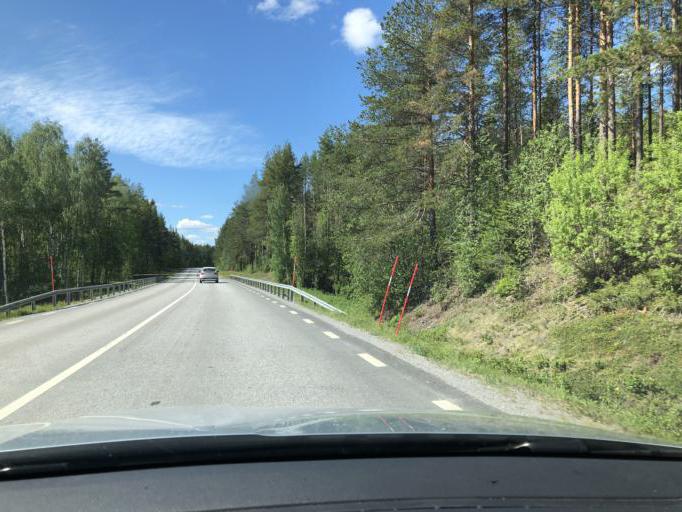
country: SE
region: Norrbotten
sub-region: Alvsbyns Kommun
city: AElvsbyn
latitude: 65.6501
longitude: 21.0998
